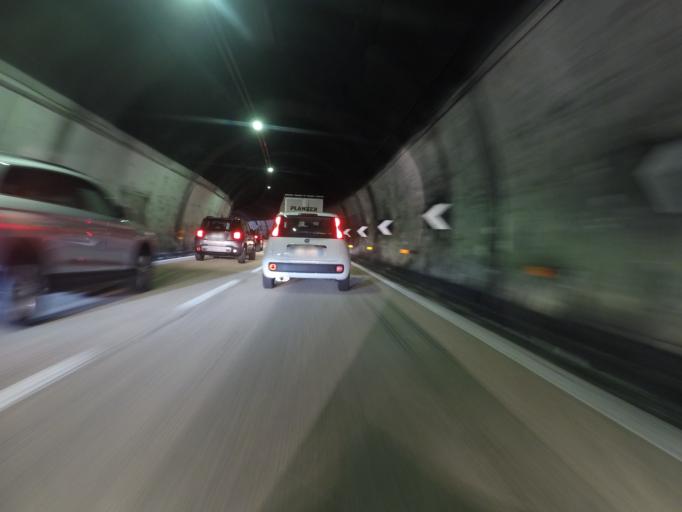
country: CH
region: Ticino
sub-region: Mendrisio District
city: Chiasso
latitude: 45.8280
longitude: 9.0418
